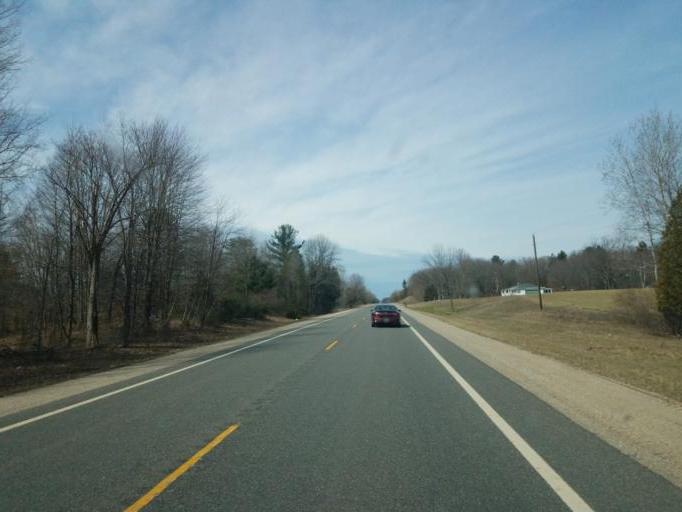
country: US
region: Michigan
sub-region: Oceana County
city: Shelby
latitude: 43.5709
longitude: -86.2629
